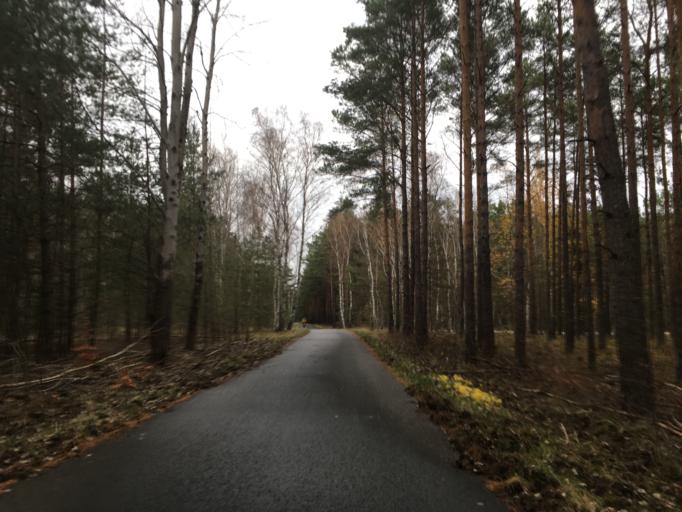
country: DE
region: Brandenburg
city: Mullrose
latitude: 52.2303
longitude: 14.4465
